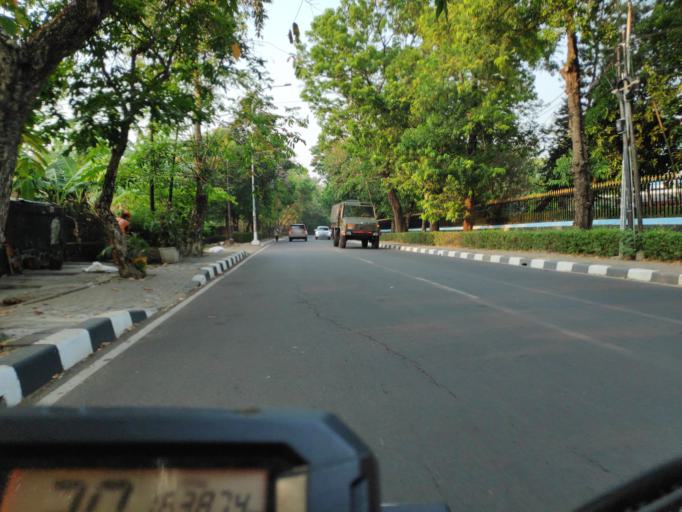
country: ID
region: Jakarta Raya
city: Jakarta
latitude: -6.2498
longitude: 106.8039
